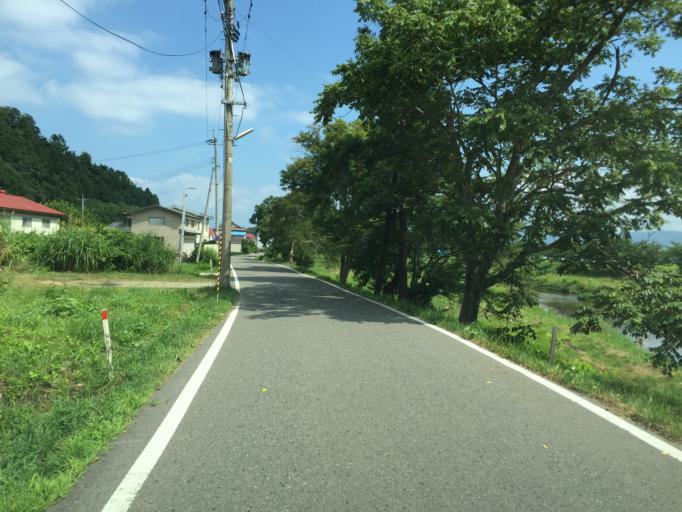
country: JP
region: Fukushima
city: Inawashiro
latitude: 37.4118
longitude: 140.1238
